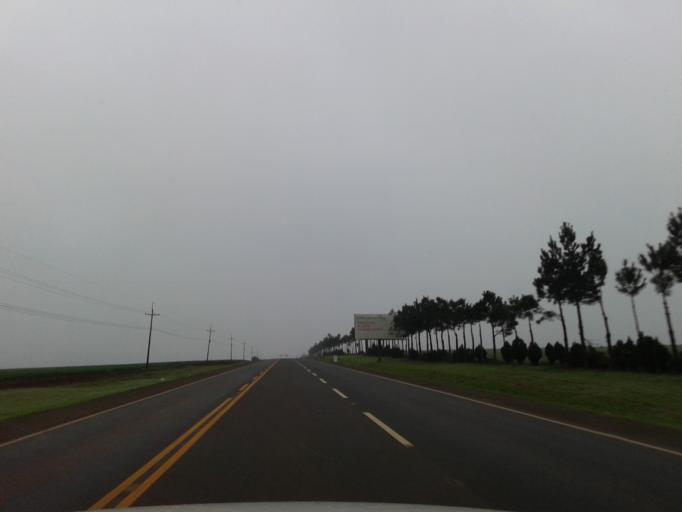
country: PY
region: Itapua
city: Pirapo
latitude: -26.9050
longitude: -55.4795
